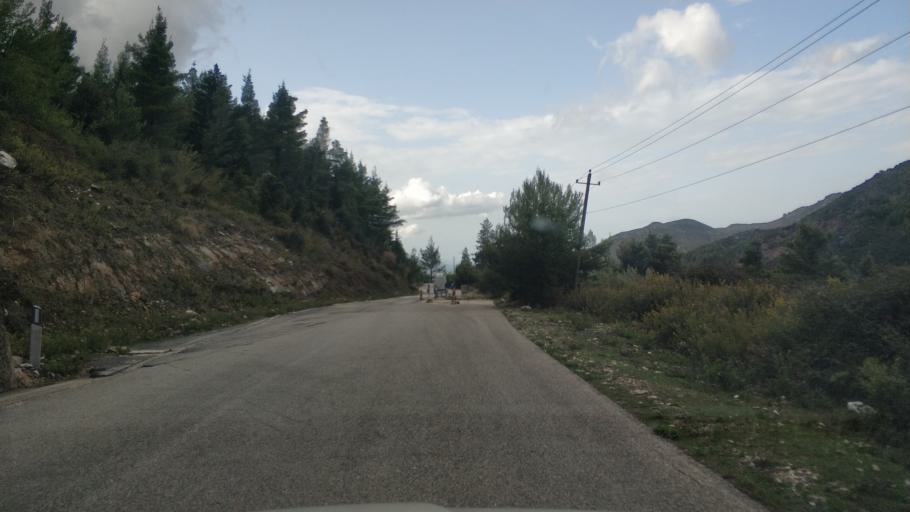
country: AL
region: Vlore
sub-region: Rrethi i Vlores
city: Orikum
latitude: 40.2577
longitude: 19.5277
